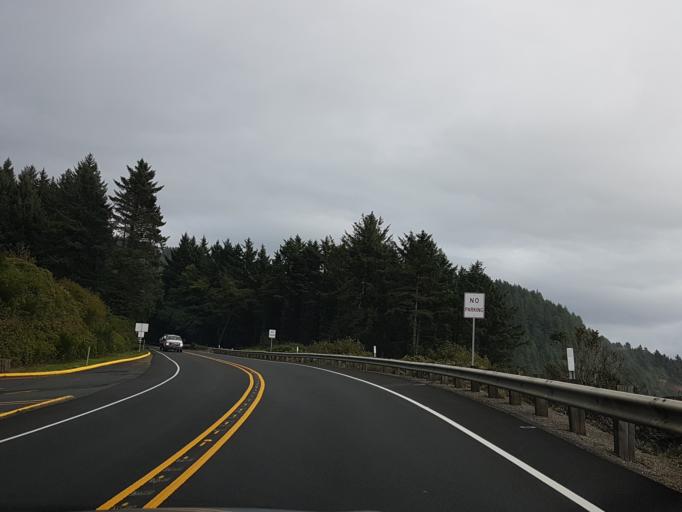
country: US
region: Oregon
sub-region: Lane County
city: Florence
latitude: 44.1212
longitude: -124.1261
